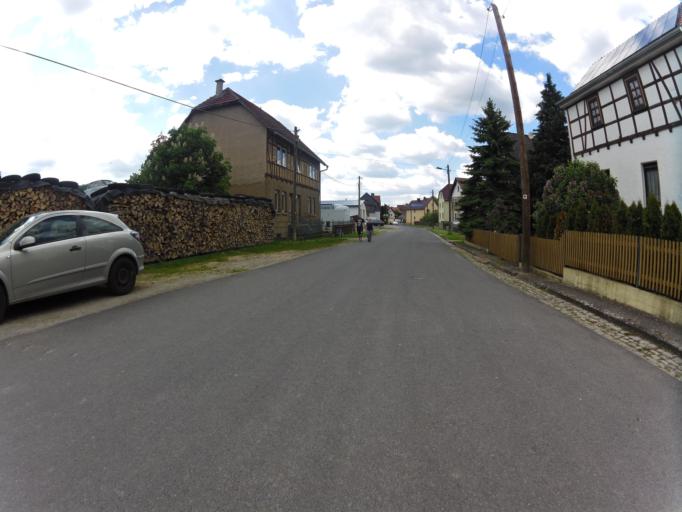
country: DE
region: Thuringia
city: Frankenroda
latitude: 51.1137
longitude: 10.2683
